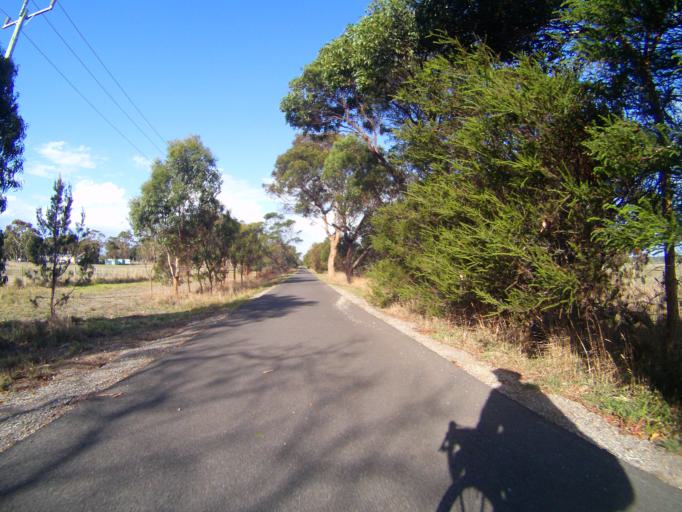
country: AU
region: Victoria
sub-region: Greater Geelong
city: Leopold
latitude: -38.1818
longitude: 144.5023
